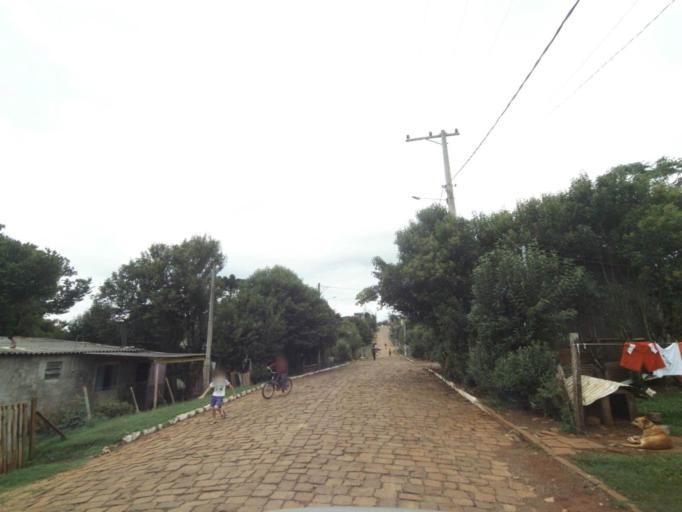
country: BR
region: Rio Grande do Sul
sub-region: Lagoa Vermelha
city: Lagoa Vermelha
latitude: -28.2248
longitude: -51.5408
